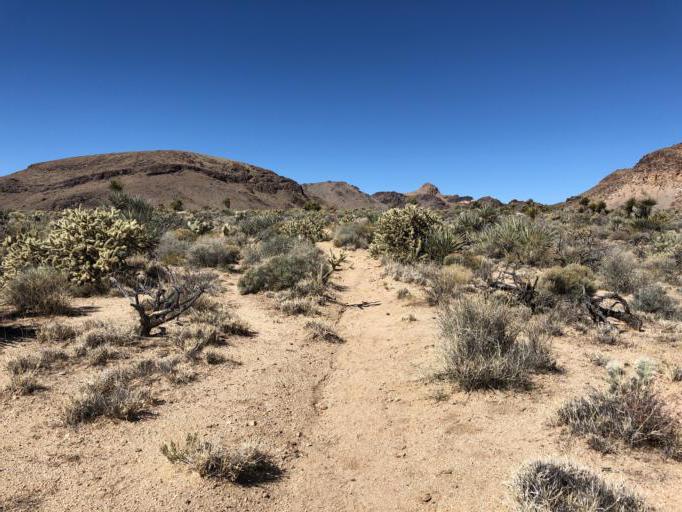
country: US
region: Nevada
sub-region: Clark County
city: Sandy Valley
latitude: 35.0398
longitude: -115.4066
